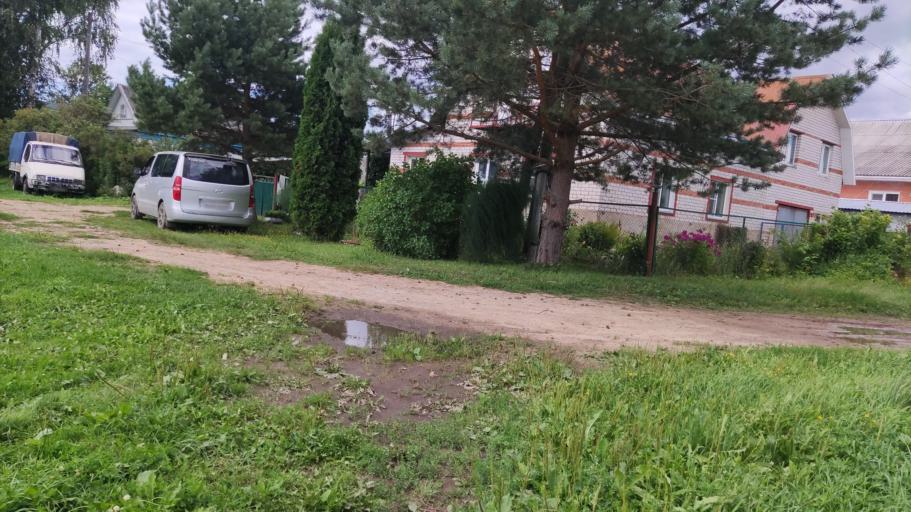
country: RU
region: Tverskaya
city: Rzhev
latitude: 56.2411
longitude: 34.2971
